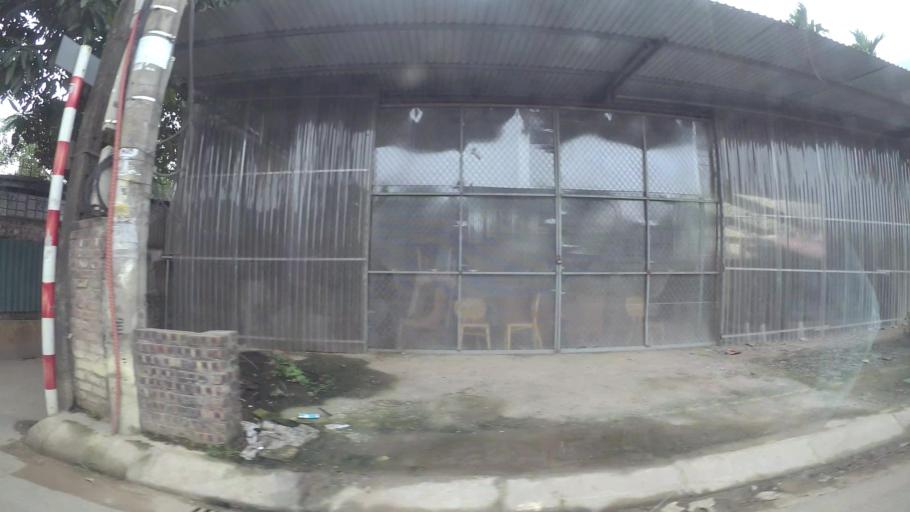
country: VN
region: Ha Noi
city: Tay Ho
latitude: 21.0735
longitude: 105.8268
